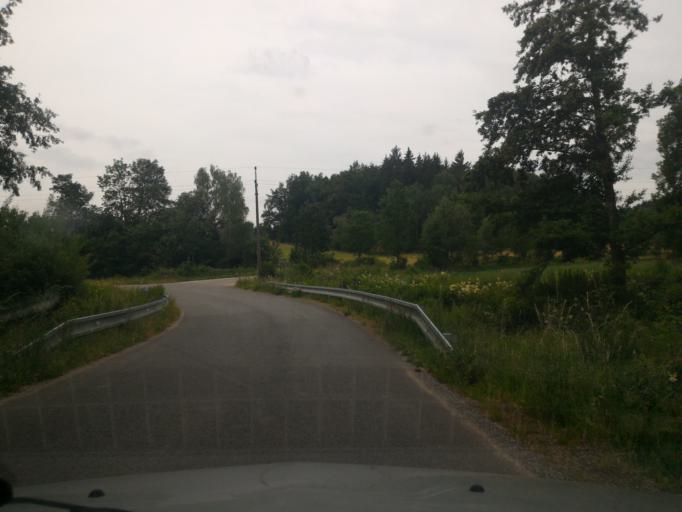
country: CZ
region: Vysocina
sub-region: Okres Jihlava
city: Telc
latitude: 49.2177
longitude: 15.3930
